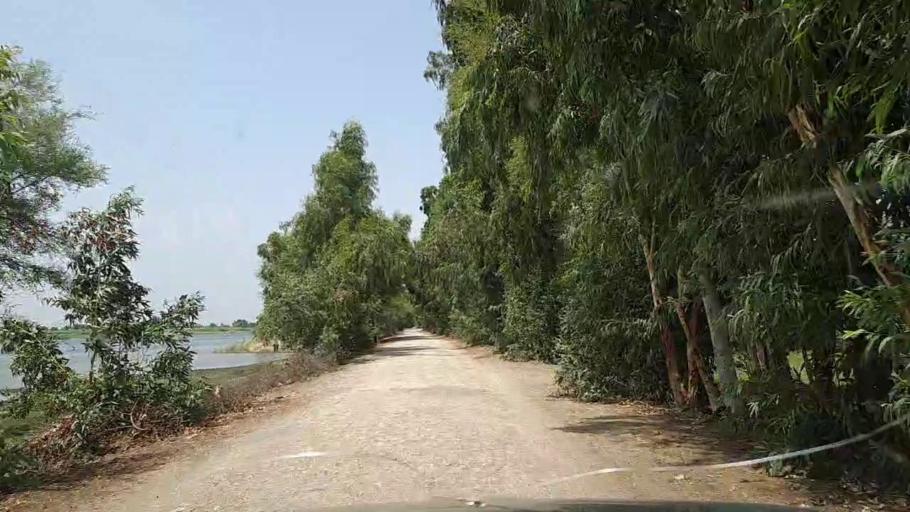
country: PK
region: Sindh
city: Ghotki
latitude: 28.0841
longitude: 69.3115
